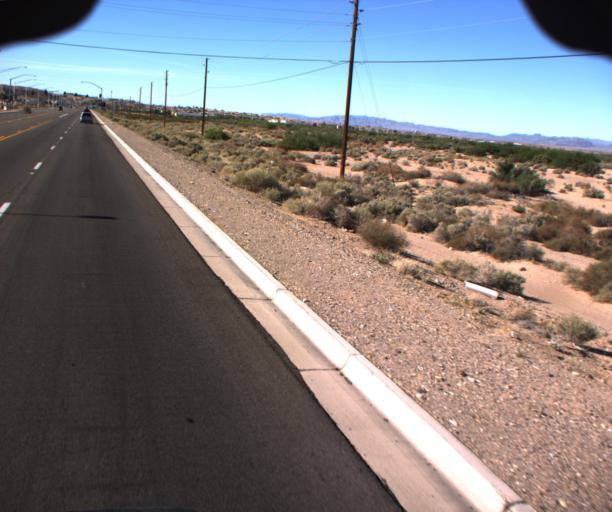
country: US
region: Arizona
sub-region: Mohave County
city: Bullhead City
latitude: 35.0644
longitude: -114.5893
